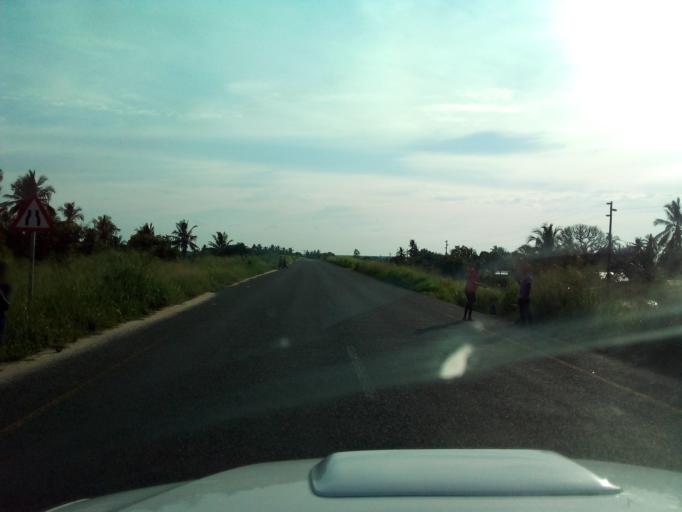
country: MZ
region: Zambezia
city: Quelimane
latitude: -17.4919
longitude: 37.0261
